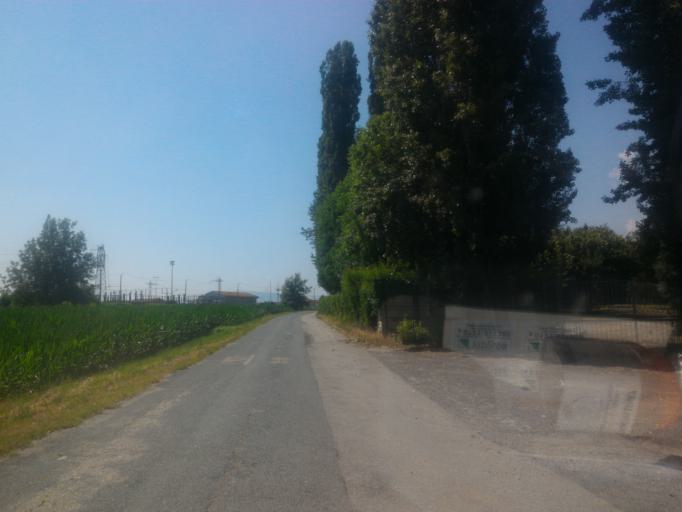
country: IT
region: Piedmont
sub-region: Provincia di Torino
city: Bricherasio
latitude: 44.8288
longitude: 7.3094
